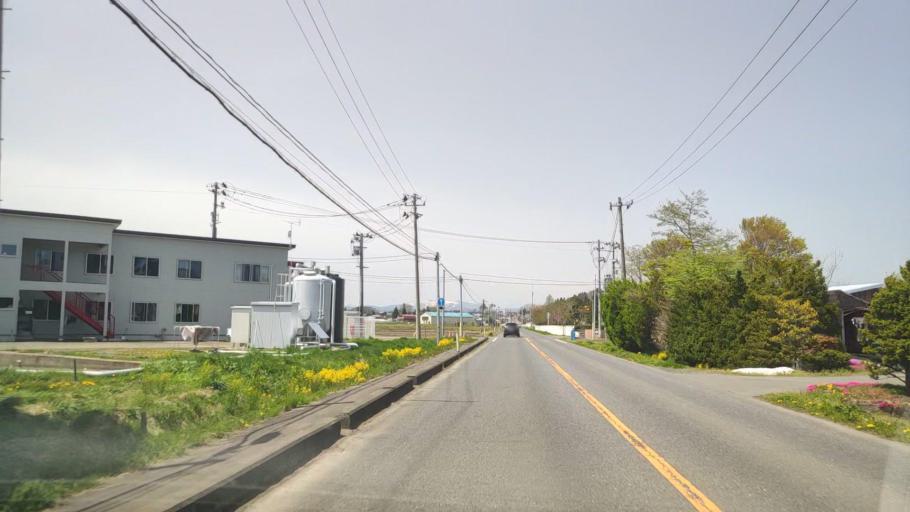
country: JP
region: Aomori
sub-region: Misawa Shi
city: Inuotose
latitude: 40.6038
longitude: 141.2962
